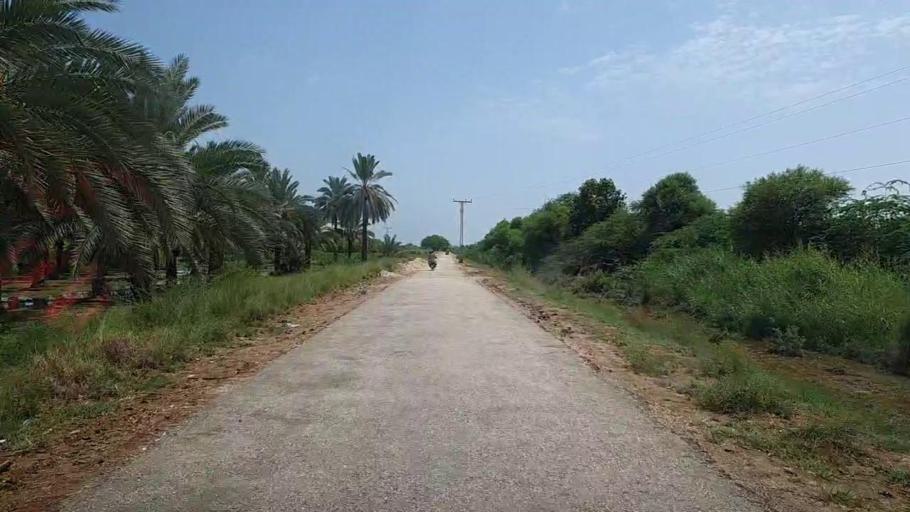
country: PK
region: Sindh
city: Bhiria
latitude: 26.9008
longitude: 68.1989
